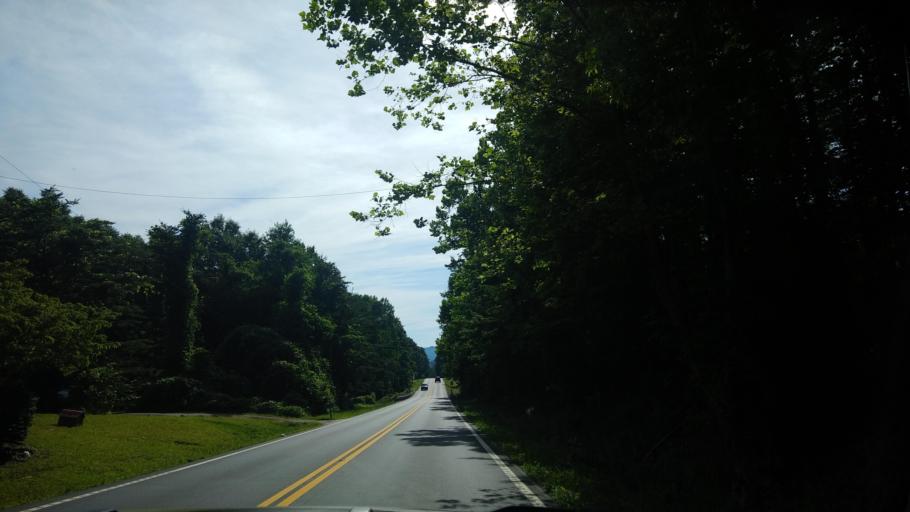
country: US
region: Tennessee
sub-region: Cocke County
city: Newport
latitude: 35.7752
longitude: -83.2562
